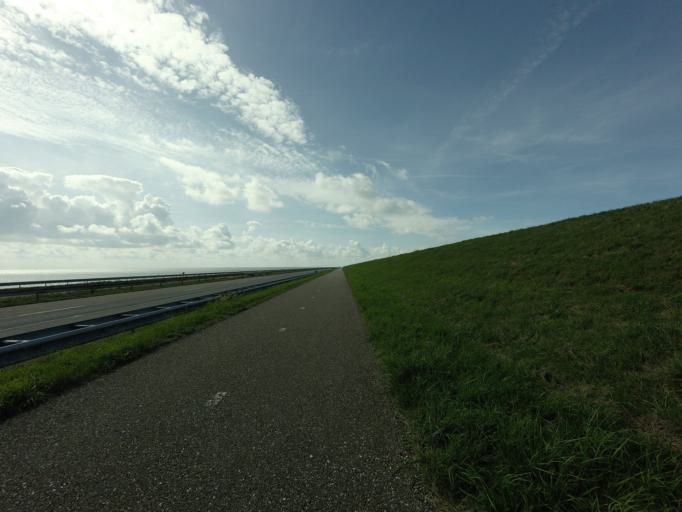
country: NL
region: North Holland
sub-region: Gemeente Hollands Kroon
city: Den Oever
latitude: 52.9982
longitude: 5.1638
